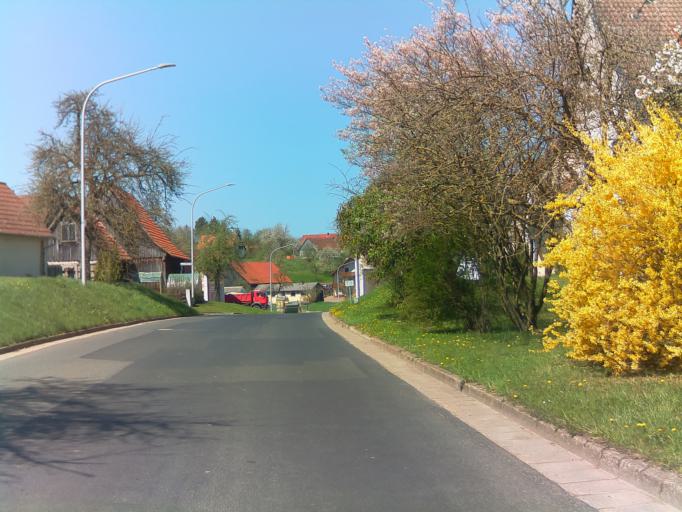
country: DE
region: Bavaria
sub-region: Upper Palatinate
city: Illschwang
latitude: 49.4351
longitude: 11.6180
